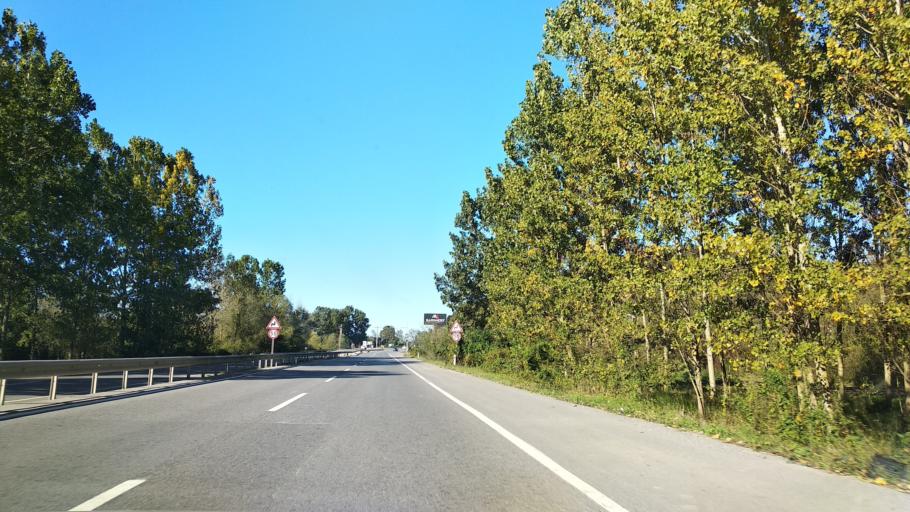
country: TR
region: Sakarya
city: Karasu
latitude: 41.0777
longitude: 30.6461
